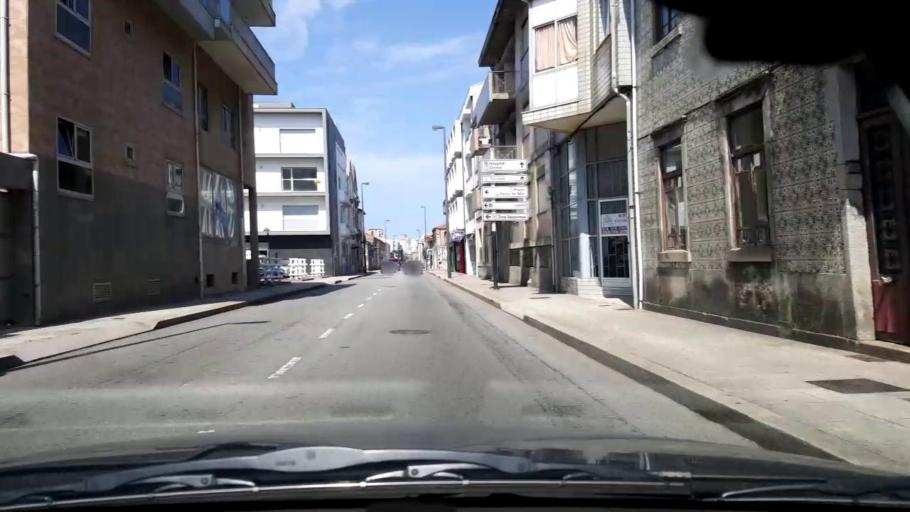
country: PT
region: Porto
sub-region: Povoa de Varzim
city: Povoa de Varzim
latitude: 41.3754
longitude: -8.7569
